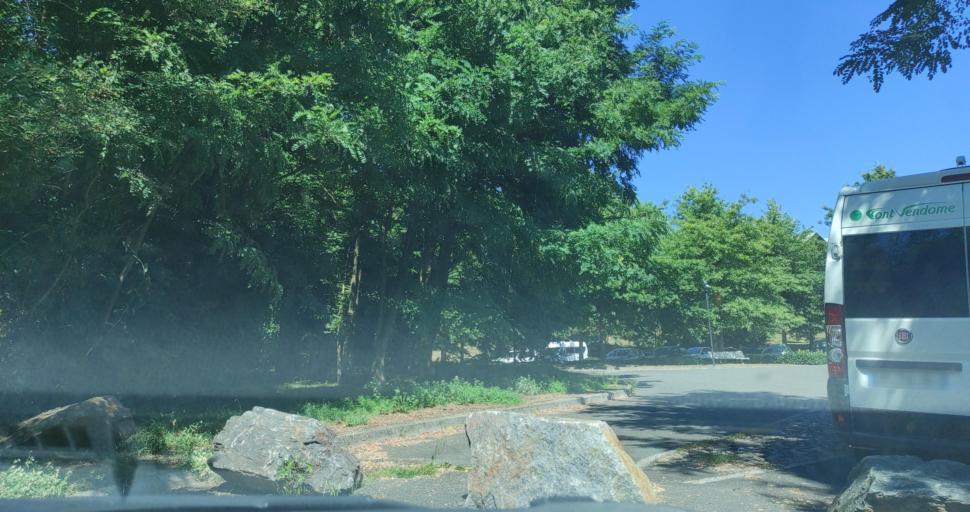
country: FR
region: Midi-Pyrenees
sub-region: Departement de l'Aveyron
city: Cransac
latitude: 44.5277
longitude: 2.2754
